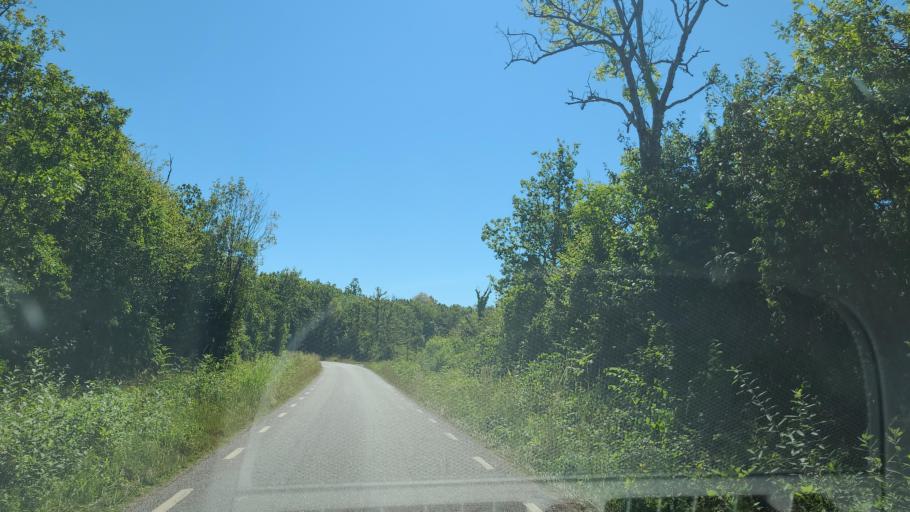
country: SE
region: Kalmar
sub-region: Borgholms Kommun
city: Borgholm
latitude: 56.7627
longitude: 16.6515
